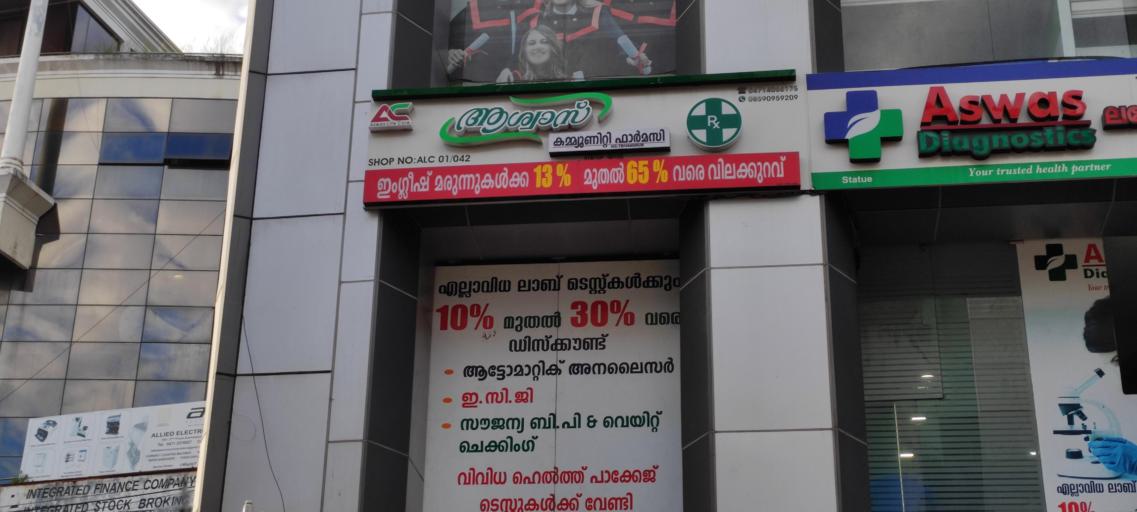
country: IN
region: Kerala
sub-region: Thiruvananthapuram
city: Thiruvananthapuram
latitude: 8.4978
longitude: 76.9482
